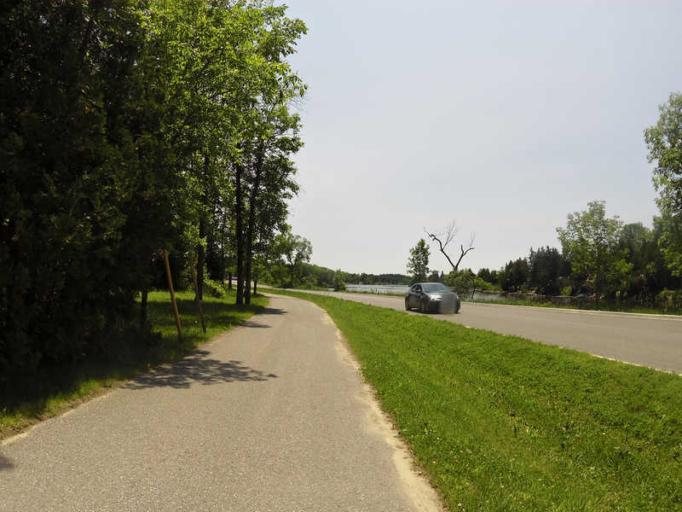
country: CA
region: Ontario
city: Peterborough
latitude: 44.4186
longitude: -78.2673
